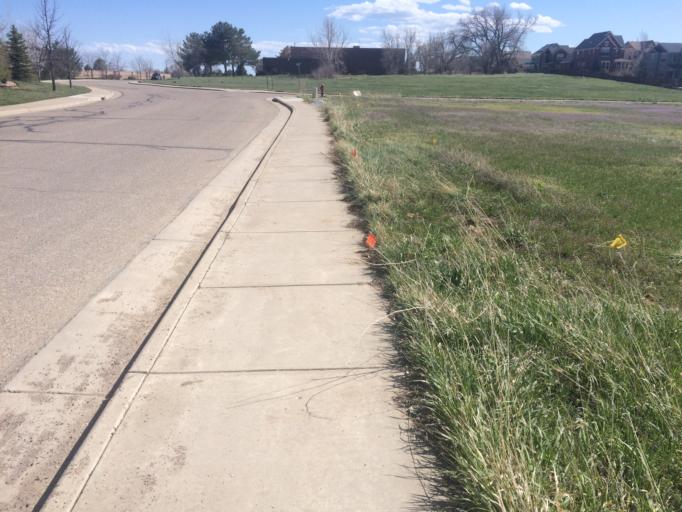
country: US
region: Colorado
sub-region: Boulder County
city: Lafayette
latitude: 40.0068
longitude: -105.1069
